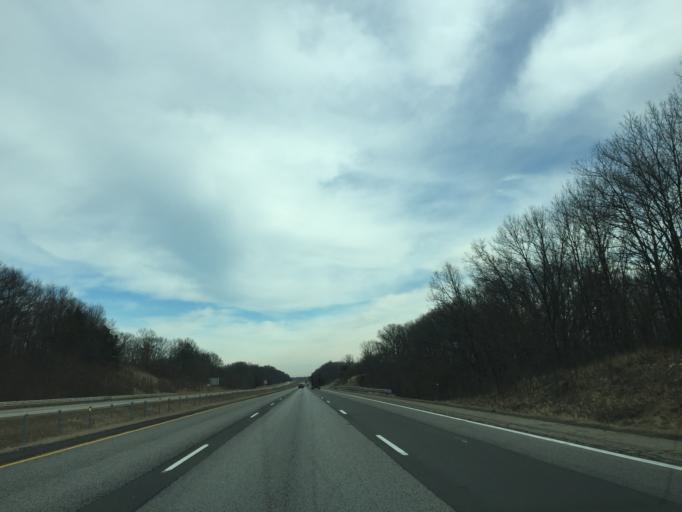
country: US
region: Michigan
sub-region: Berrien County
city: Bridgman
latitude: 41.9481
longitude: -86.5636
